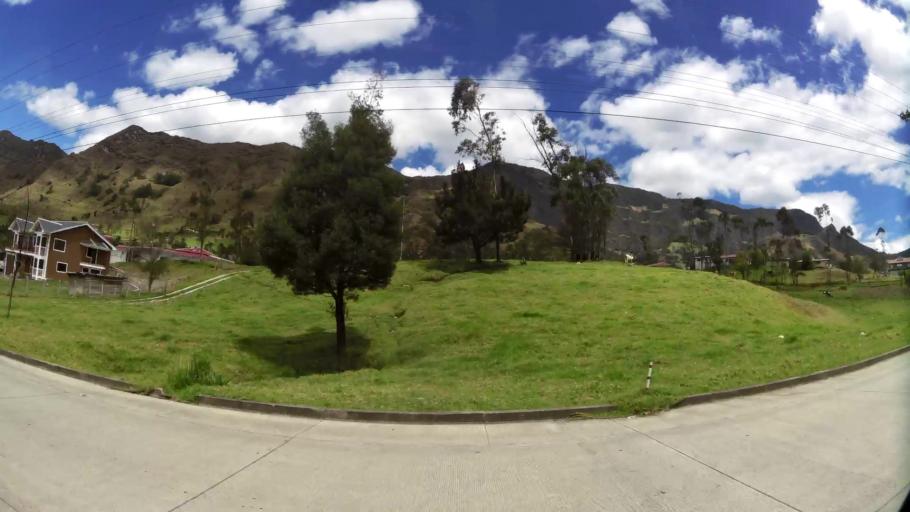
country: EC
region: Azuay
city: Cuenca
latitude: -3.1373
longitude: -79.1343
